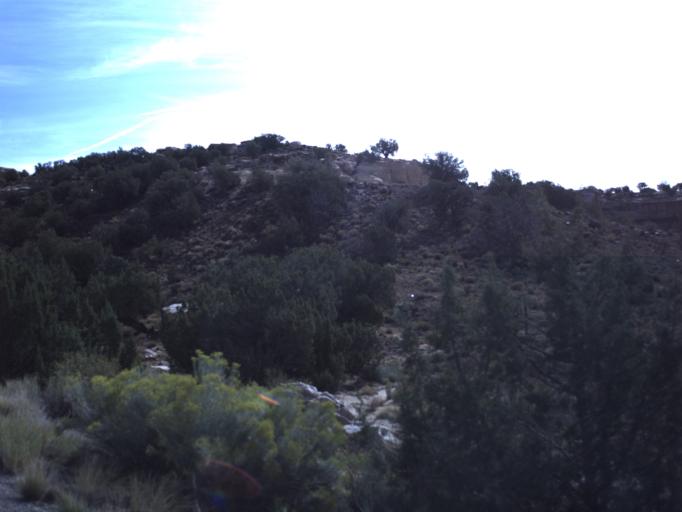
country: US
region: Utah
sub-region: San Juan County
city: Blanding
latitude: 37.4345
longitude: -109.3939
